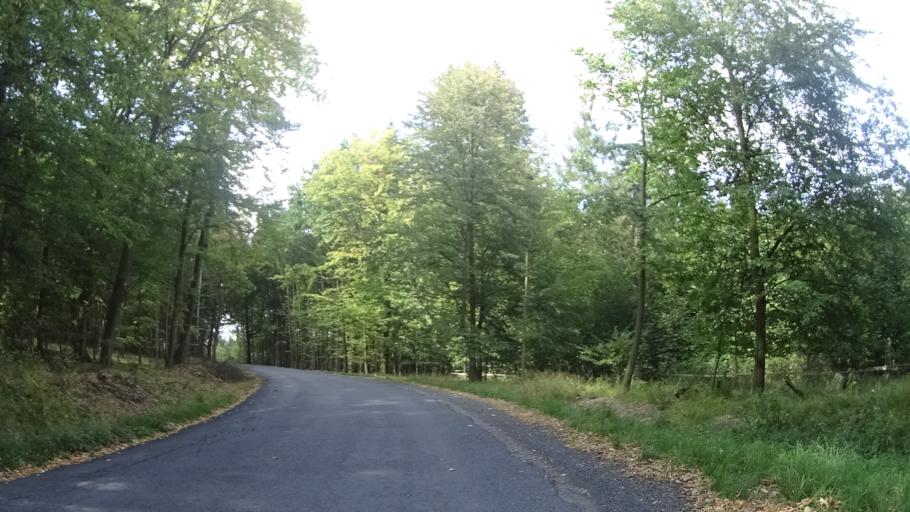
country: CZ
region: Olomoucky
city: Bila Lhota
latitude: 49.7307
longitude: 17.0096
